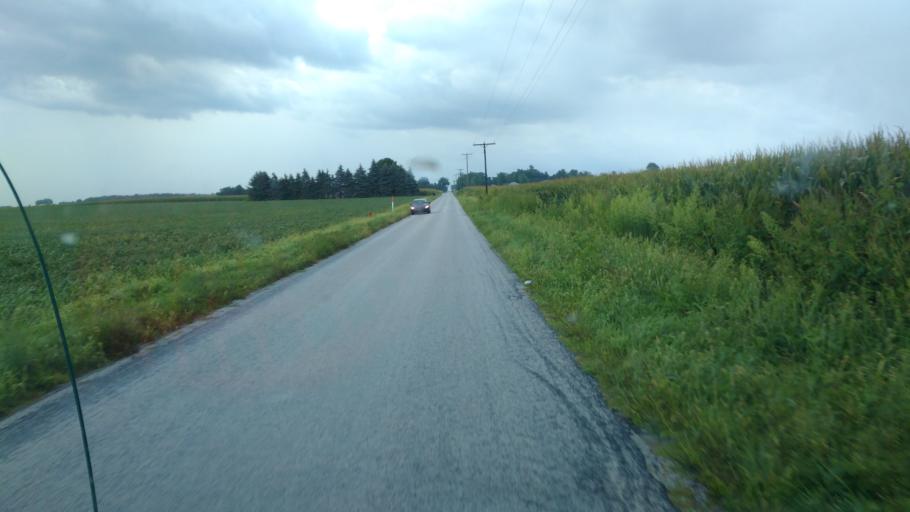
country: US
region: Ohio
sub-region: Hardin County
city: Kenton
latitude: 40.6739
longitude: -83.5888
